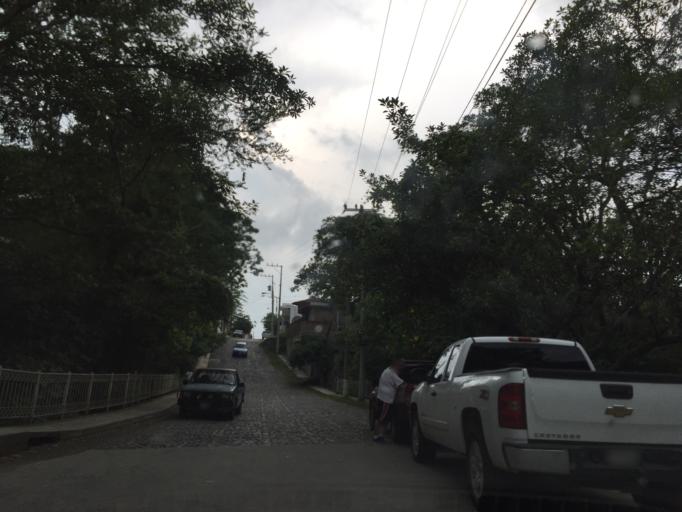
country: MX
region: Colima
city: Comala
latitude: 19.3279
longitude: -103.7578
